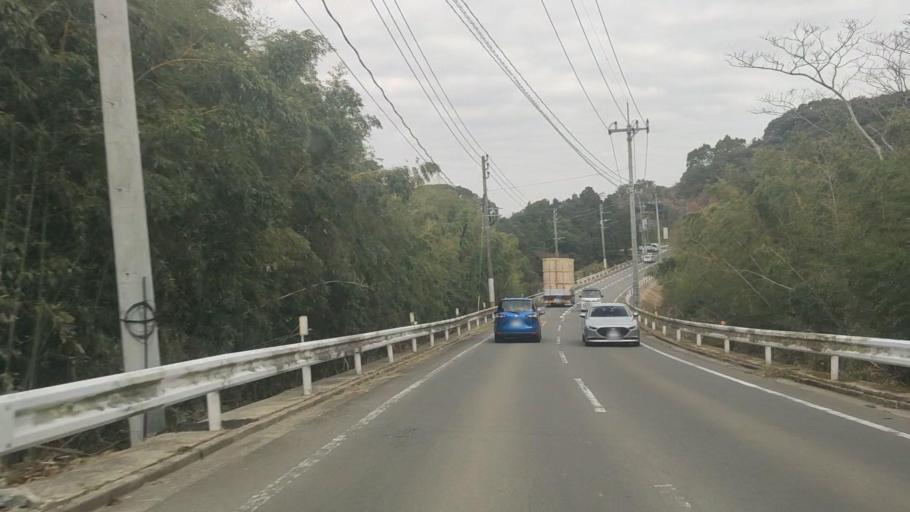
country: JP
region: Nagasaki
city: Shimabara
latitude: 32.8445
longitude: 130.2149
